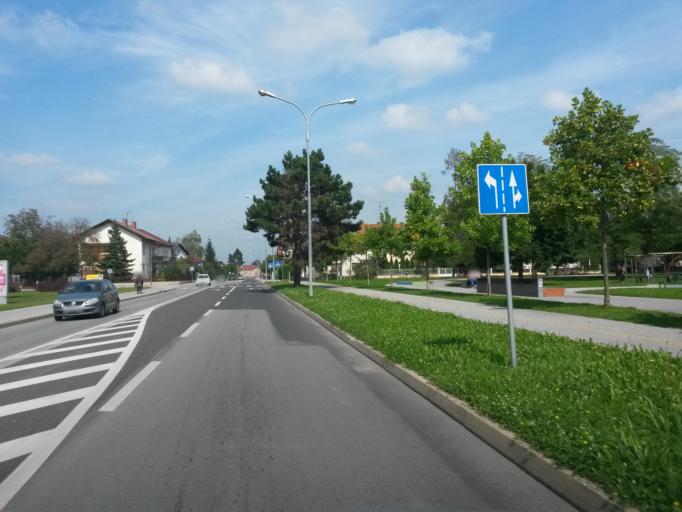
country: HR
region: Varazdinska
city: Varazdin
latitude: 46.3115
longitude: 16.3269
